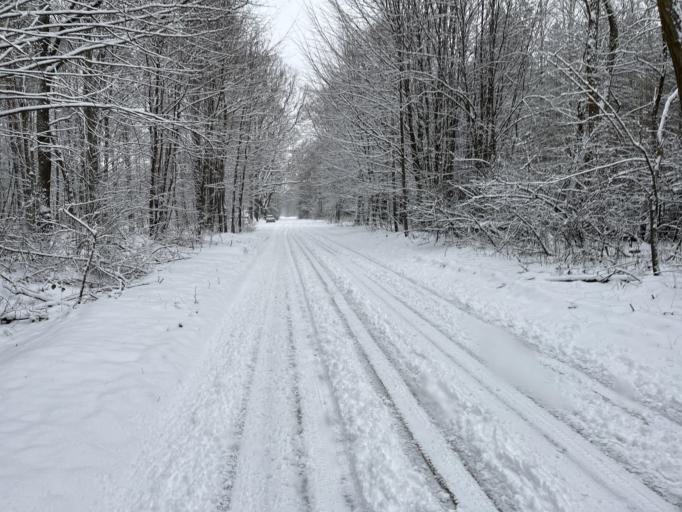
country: PL
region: Masovian Voivodeship
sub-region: Powiat zyrardowski
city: Guzow
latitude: 52.0478
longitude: 20.2730
